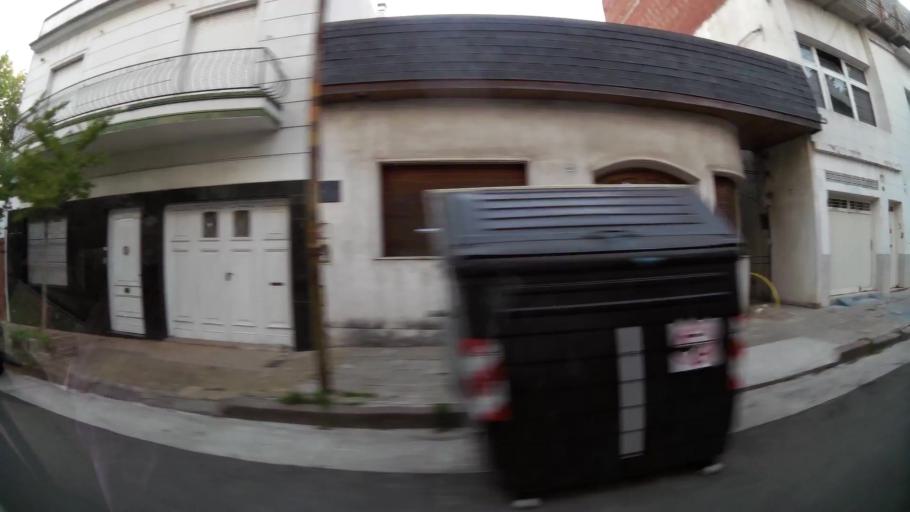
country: AR
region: Buenos Aires F.D.
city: Colegiales
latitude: -34.5482
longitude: -58.4749
